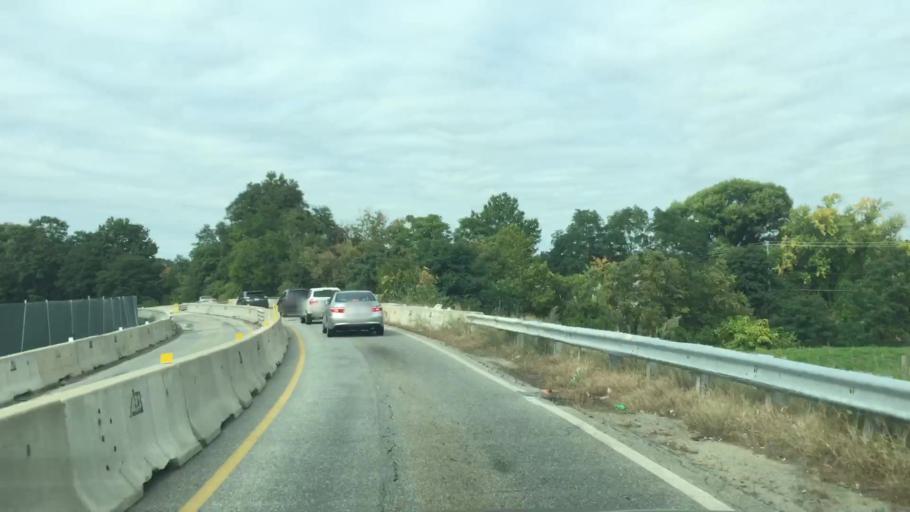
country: US
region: Massachusetts
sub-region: Middlesex County
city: Dracut
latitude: 42.6591
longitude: -71.3178
